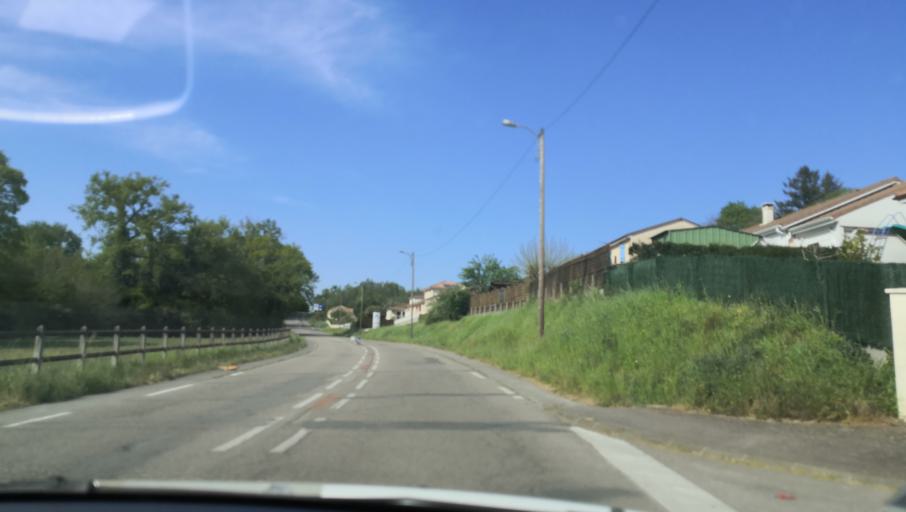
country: FR
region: Limousin
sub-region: Departement de la Haute-Vienne
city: Couzeix
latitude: 45.8627
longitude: 1.2588
